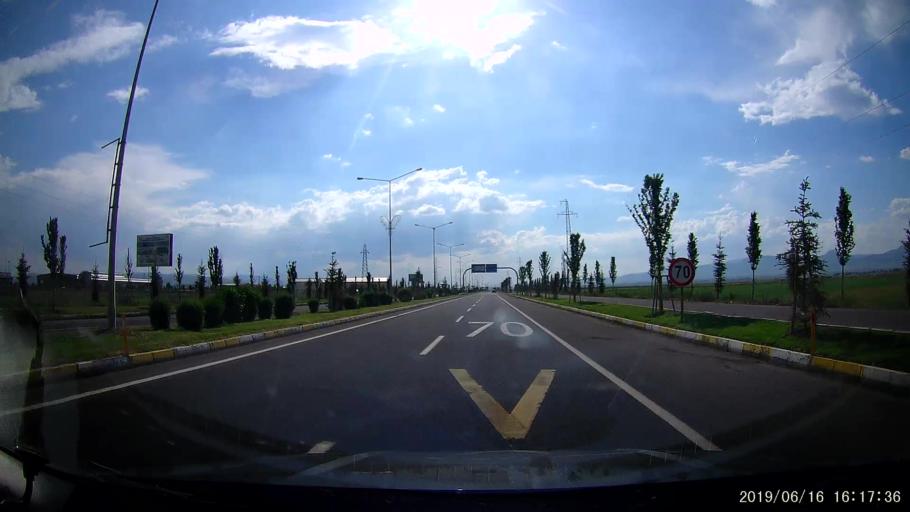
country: TR
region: Erzurum
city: Ilica
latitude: 39.9641
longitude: 41.1834
